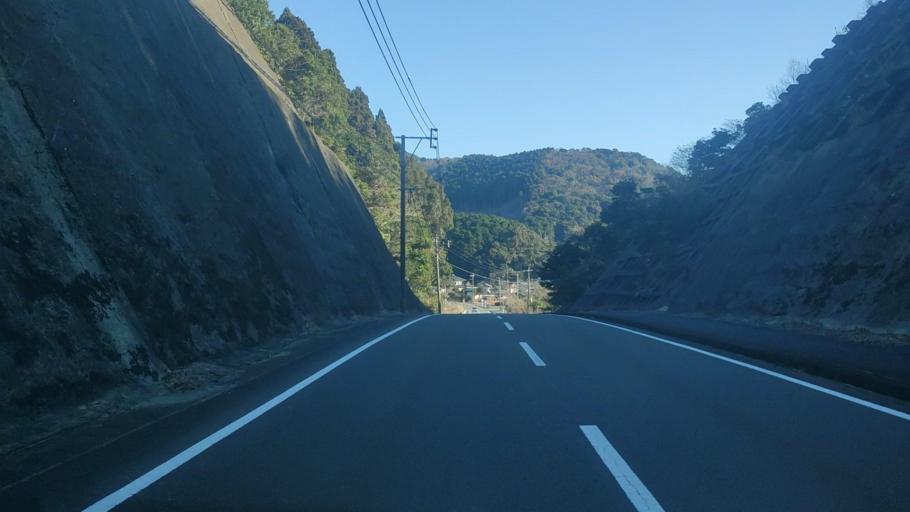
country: JP
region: Miyazaki
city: Nobeoka
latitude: 32.6873
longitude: 131.8051
